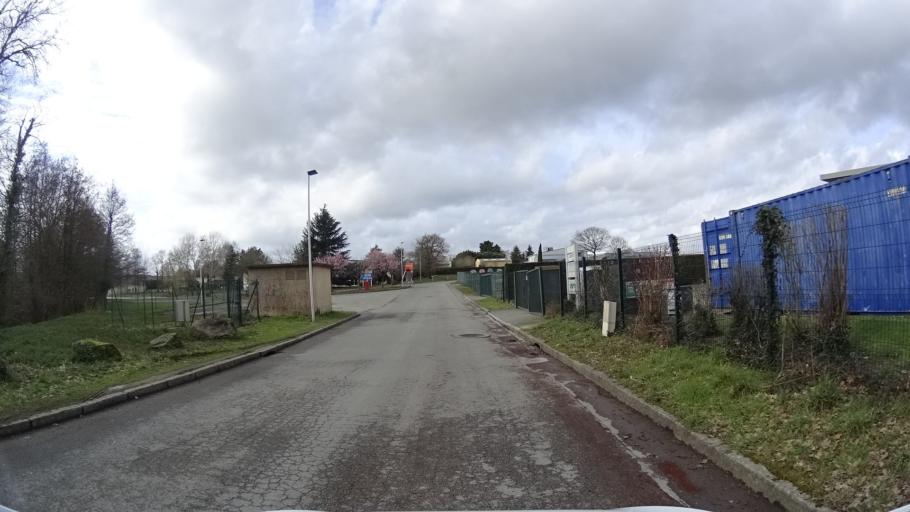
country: FR
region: Brittany
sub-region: Departement d'Ille-et-Vilaine
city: Saint-Gilles
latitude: 48.1559
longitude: -1.8169
